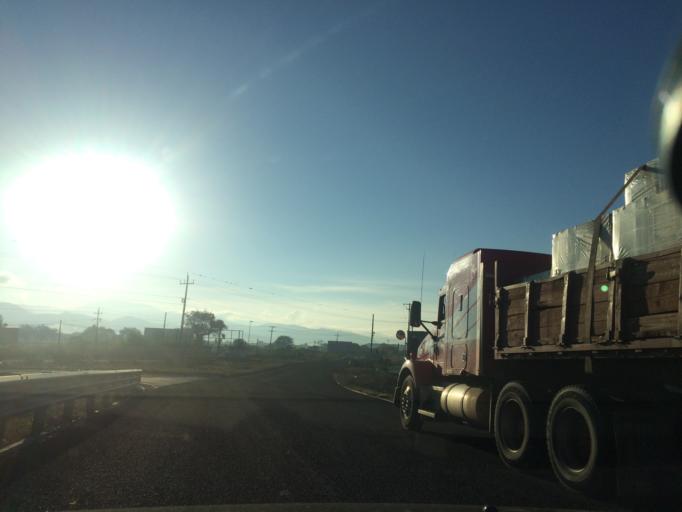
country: MX
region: Puebla
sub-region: Santiago Miahuatlan
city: San Jose Monte Chiquito
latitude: 18.4857
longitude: -97.4550
